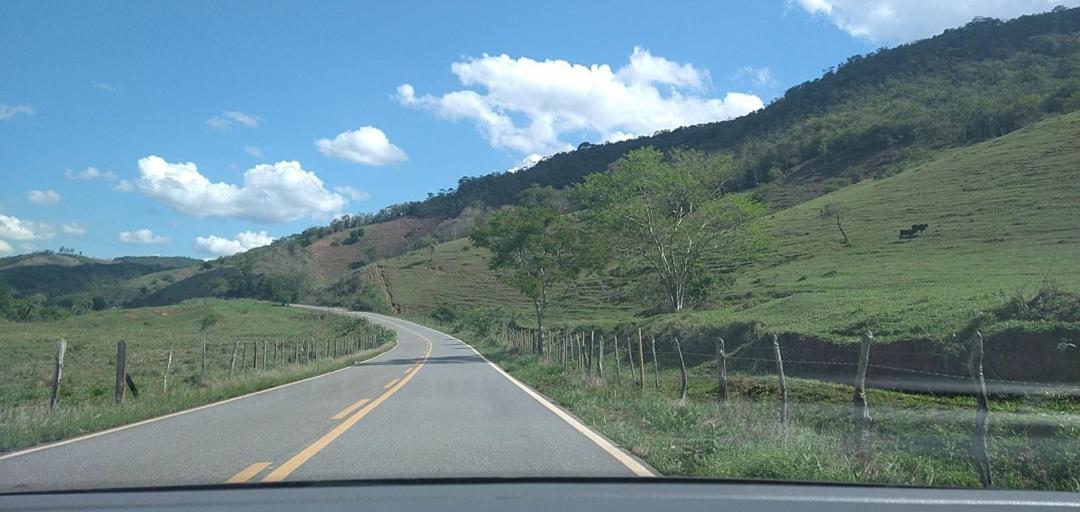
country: BR
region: Minas Gerais
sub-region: Rio Piracicaba
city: Rio Piracicaba
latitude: -19.9857
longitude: -43.1224
